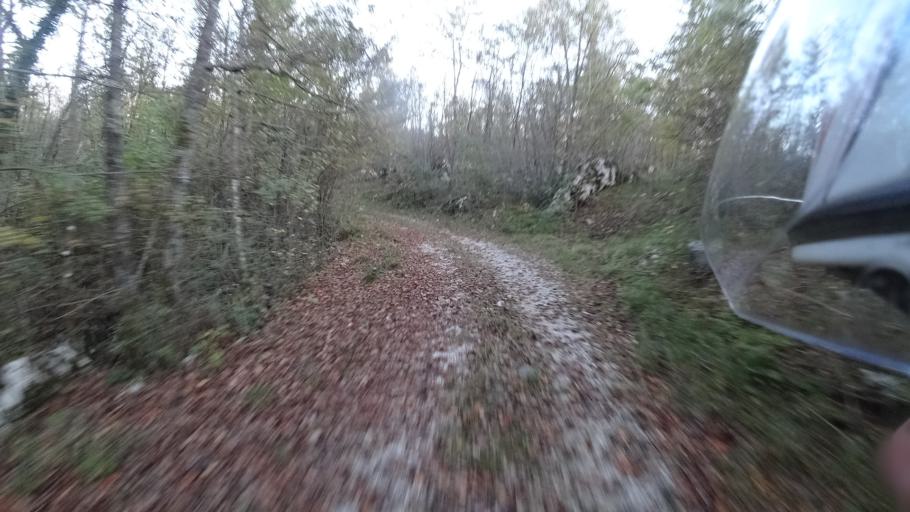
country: HR
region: Primorsko-Goranska
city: Matulji
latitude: 45.4048
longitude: 14.3103
